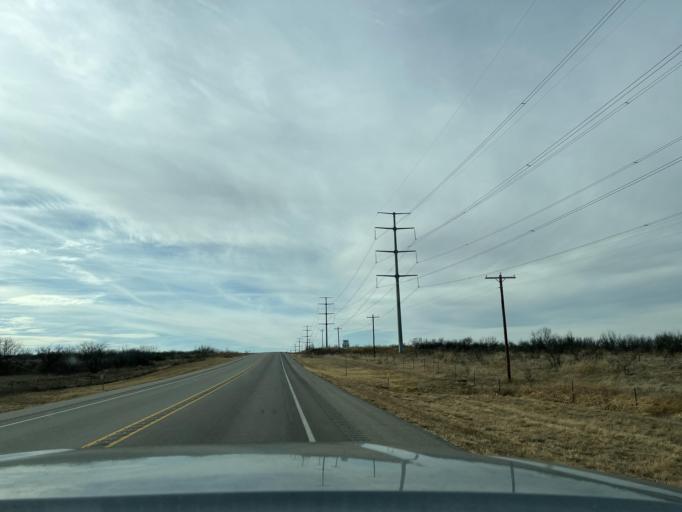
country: US
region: Texas
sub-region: Jones County
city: Stamford
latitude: 32.7503
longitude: -99.6384
